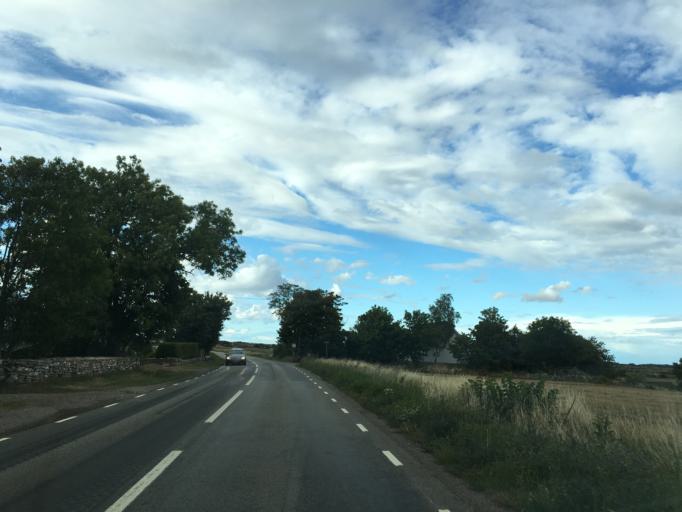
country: SE
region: Kalmar
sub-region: Morbylanga Kommun
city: Moerbylanga
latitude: 56.3908
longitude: 16.4368
